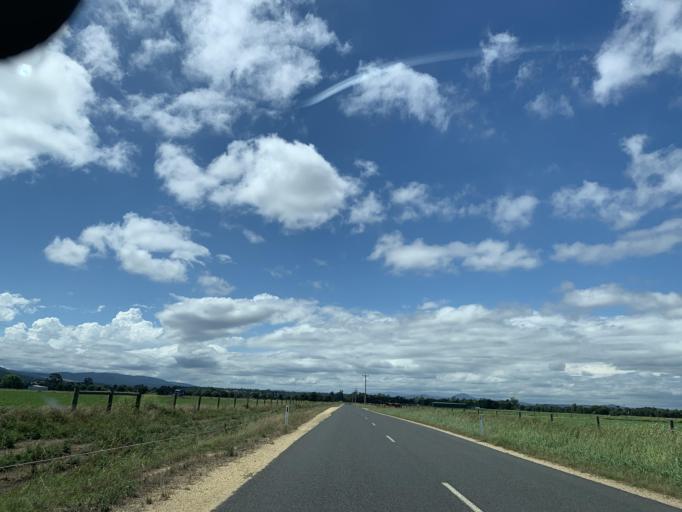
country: AU
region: Victoria
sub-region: Wellington
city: Heyfield
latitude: -37.9969
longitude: 146.6918
